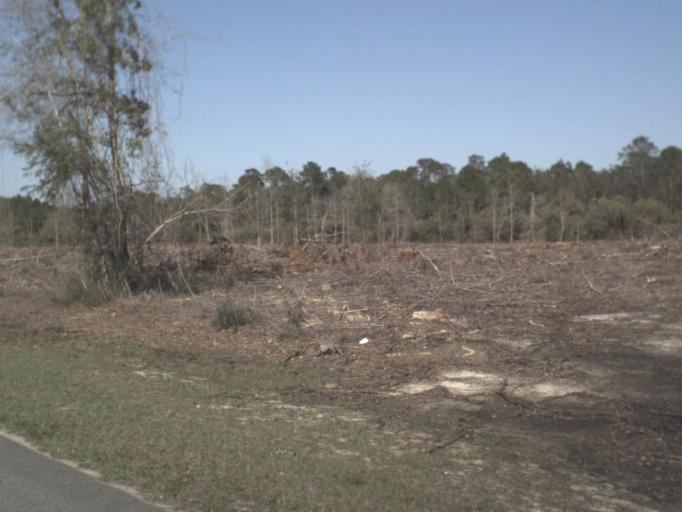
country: US
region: Florida
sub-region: Gulf County
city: Wewahitchka
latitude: 30.1623
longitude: -85.2092
